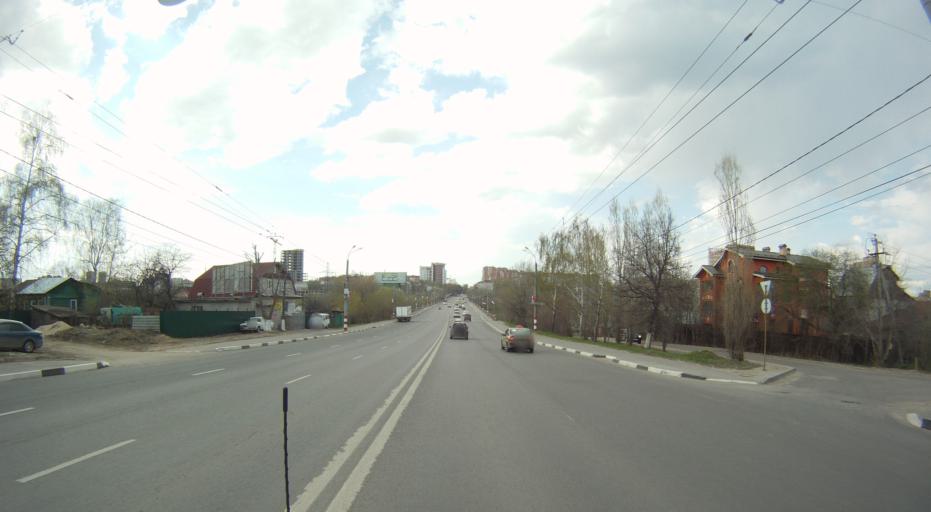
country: RU
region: Nizjnij Novgorod
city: Nizhniy Novgorod
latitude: 56.3040
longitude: 44.0279
